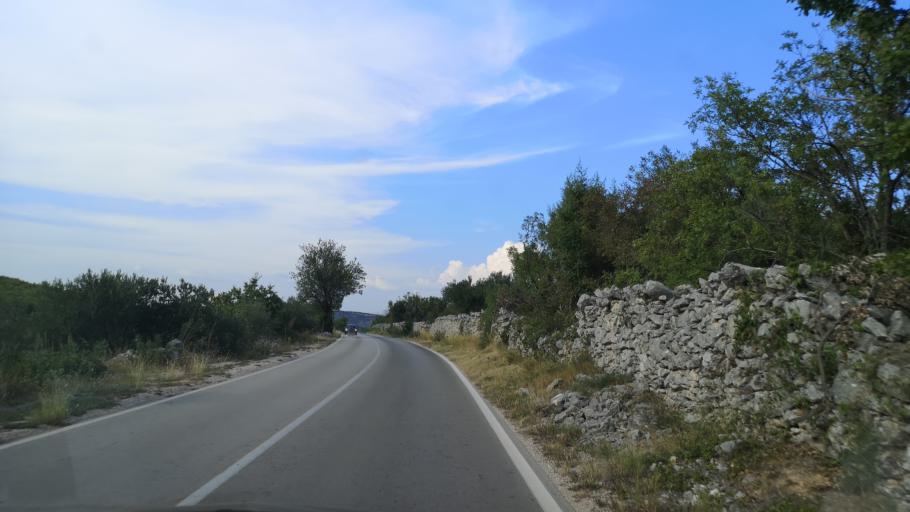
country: HR
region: Sibensko-Kniniska
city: Vodice
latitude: 43.8014
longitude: 15.7726
